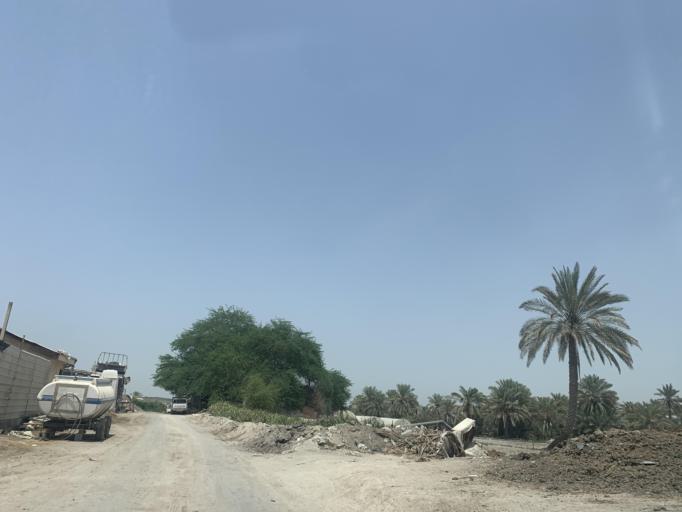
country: BH
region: Central Governorate
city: Madinat Hamad
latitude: 26.1550
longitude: 50.4986
